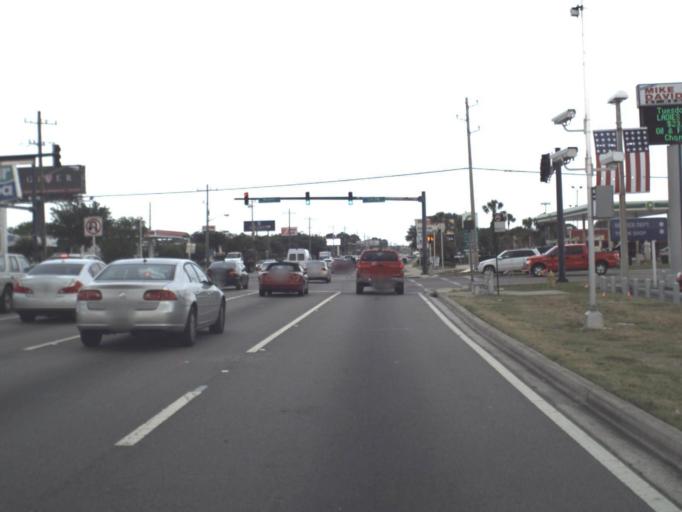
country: US
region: Florida
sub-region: Duval County
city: Jacksonville
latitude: 30.3218
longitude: -81.5475
